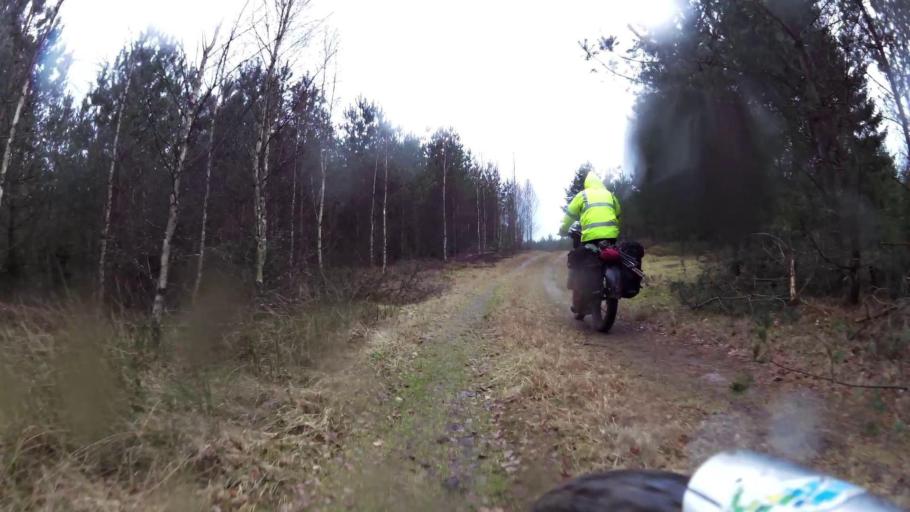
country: PL
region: Pomeranian Voivodeship
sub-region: Powiat bytowski
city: Trzebielino
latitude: 54.0774
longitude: 17.1055
